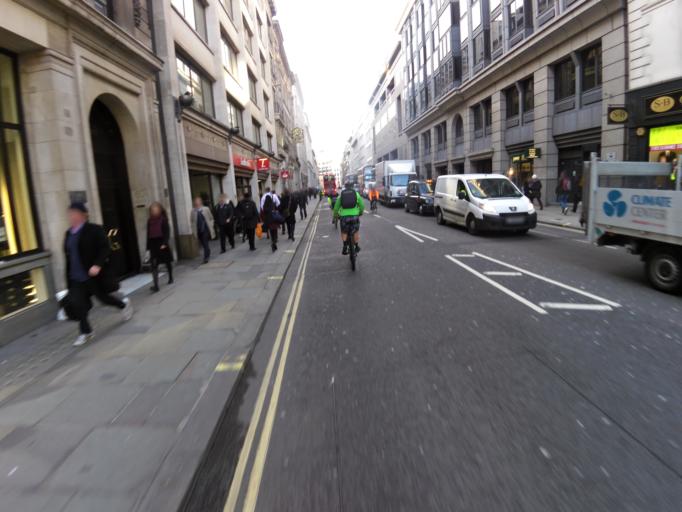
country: GB
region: England
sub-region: Greater London
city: City of London
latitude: 51.5171
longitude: -0.0887
